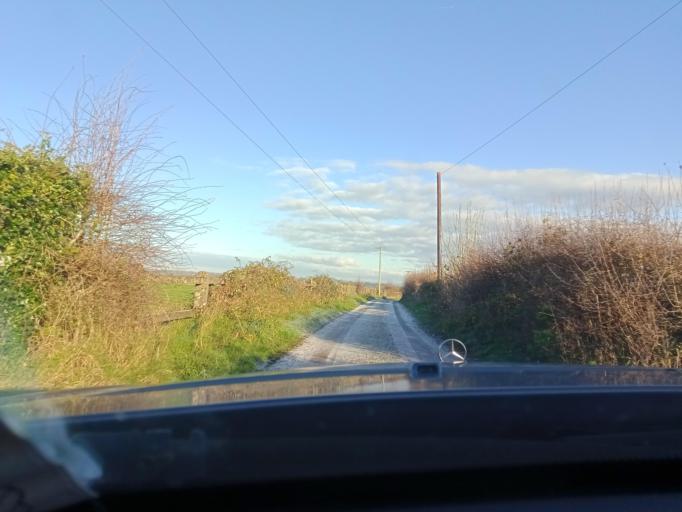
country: IE
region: Leinster
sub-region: Kilkenny
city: Graiguenamanagh
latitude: 52.5624
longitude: -6.9416
